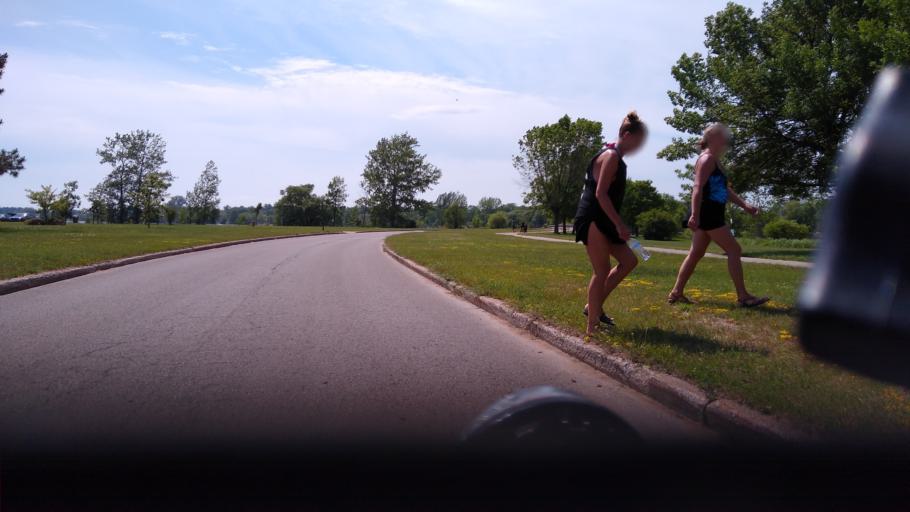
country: US
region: Michigan
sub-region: Delta County
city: Escanaba
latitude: 45.7394
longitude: -87.0465
